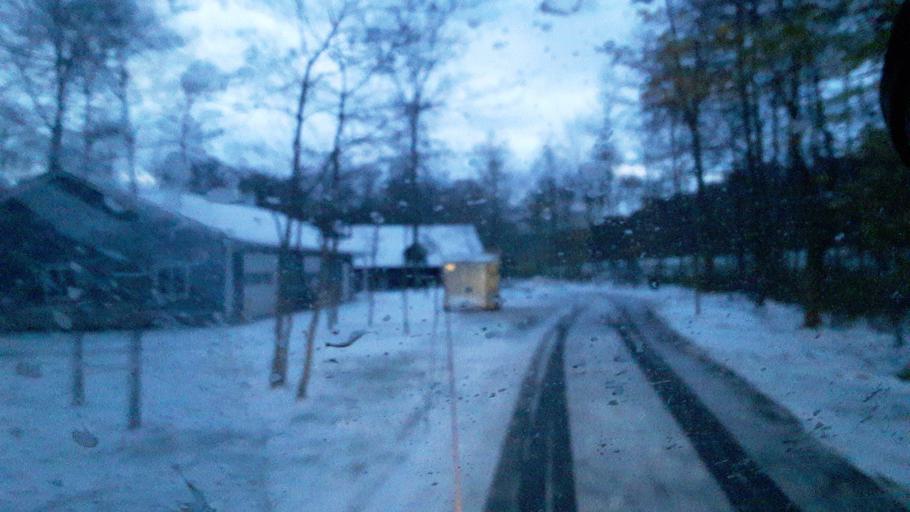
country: US
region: Ohio
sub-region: Portage County
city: Hiram
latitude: 41.3629
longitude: -81.1527
